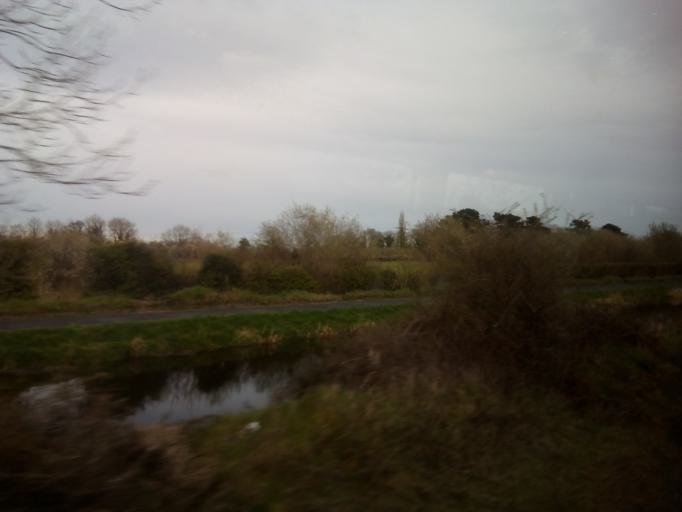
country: IE
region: Leinster
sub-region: Kildare
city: Maynooth
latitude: 53.3849
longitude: -6.6333
